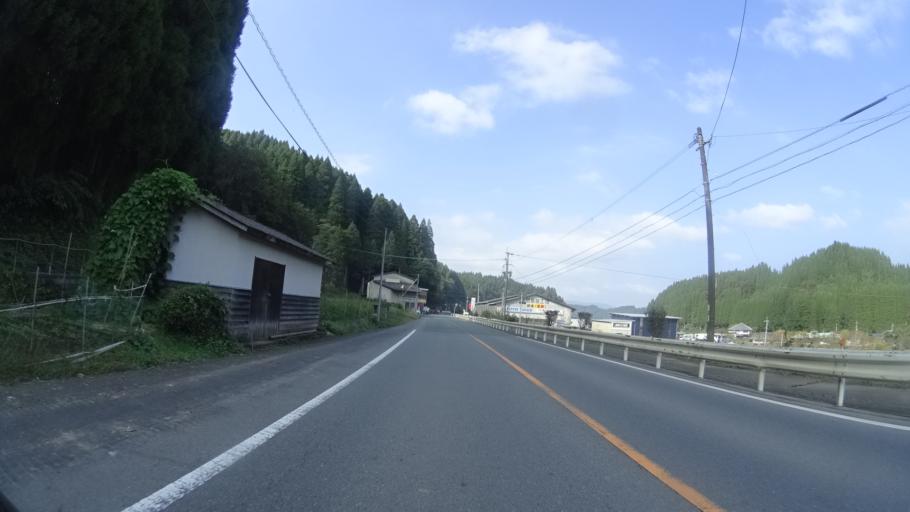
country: JP
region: Kumamoto
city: Aso
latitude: 33.0896
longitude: 131.0677
